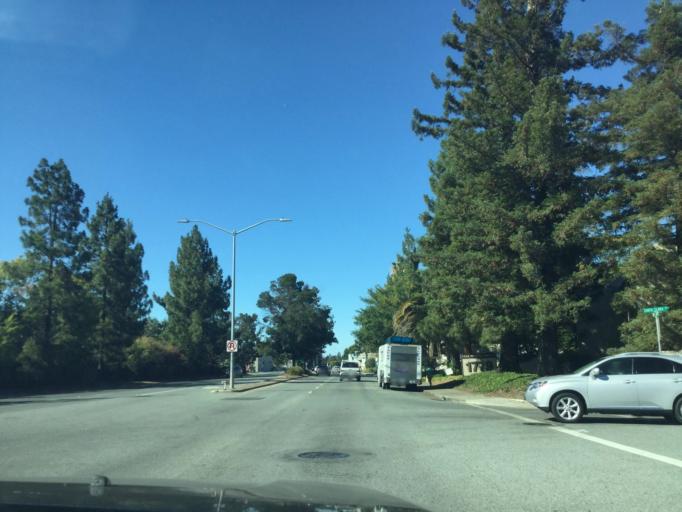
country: US
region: California
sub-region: San Mateo County
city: Atherton
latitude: 37.4532
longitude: -122.2293
